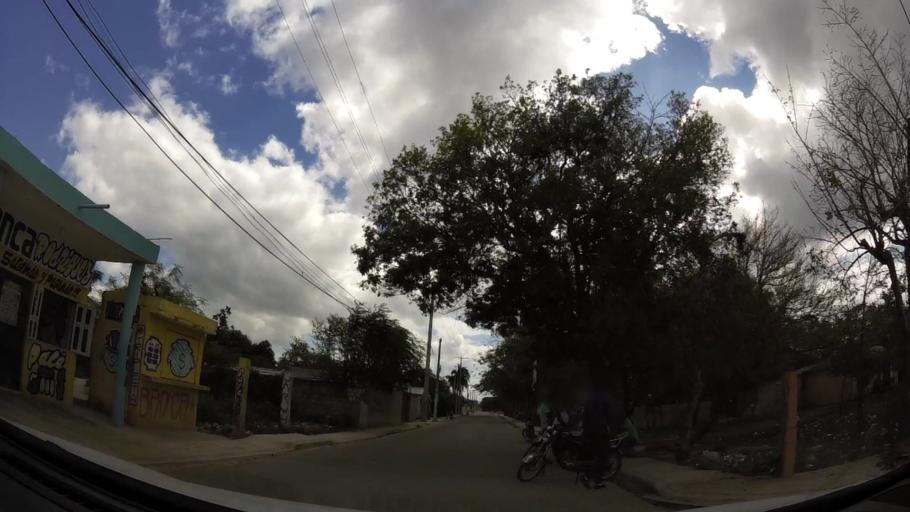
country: DO
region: Santo Domingo
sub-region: Santo Domingo
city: Boca Chica
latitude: 18.4531
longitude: -69.6433
